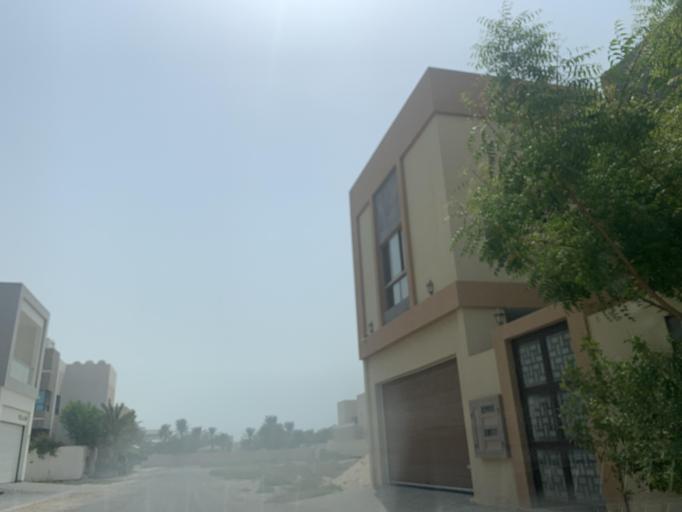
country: BH
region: Manama
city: Jidd Hafs
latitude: 26.2000
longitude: 50.4678
